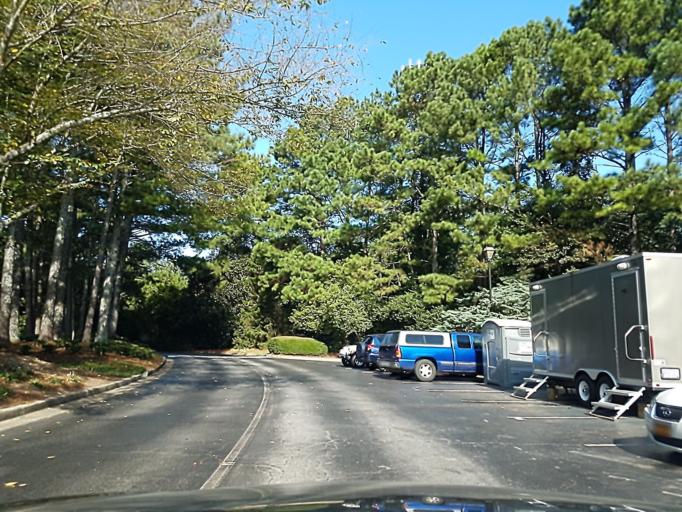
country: US
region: Georgia
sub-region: DeKalb County
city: North Druid Hills
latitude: 33.8106
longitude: -84.2939
